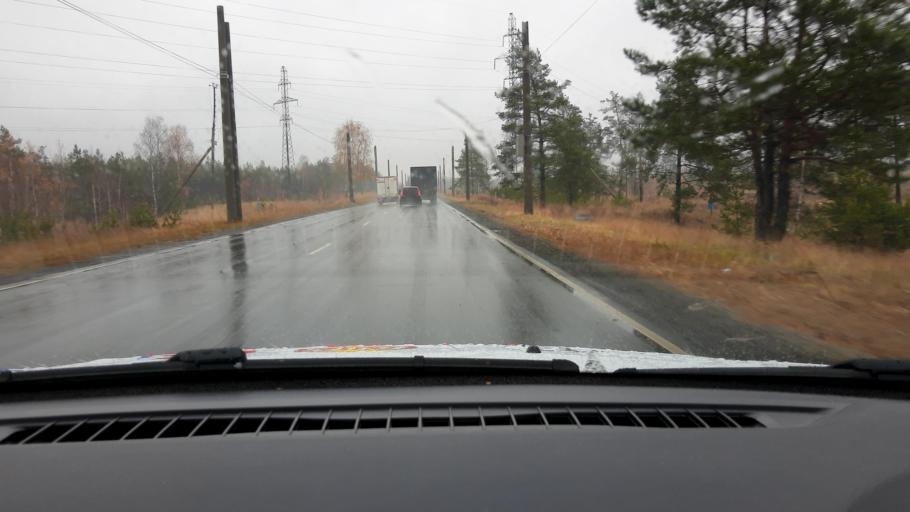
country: RU
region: Nizjnij Novgorod
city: Babino
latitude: 56.2834
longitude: 43.5773
